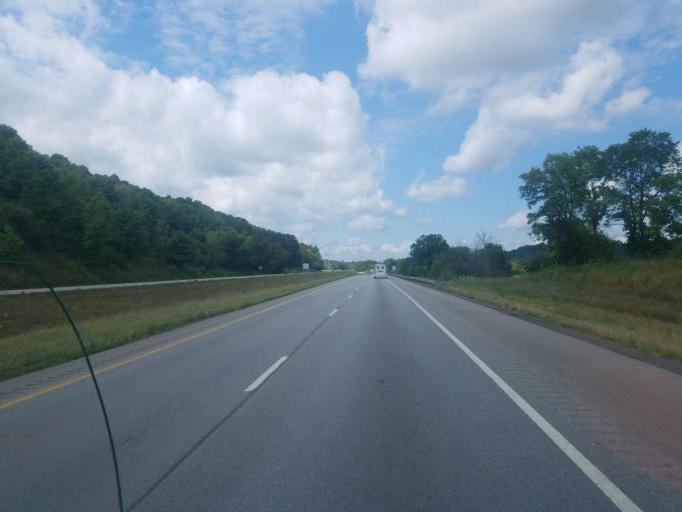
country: US
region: Ohio
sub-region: Guernsey County
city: Cambridge
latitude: 40.0077
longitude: -81.6503
